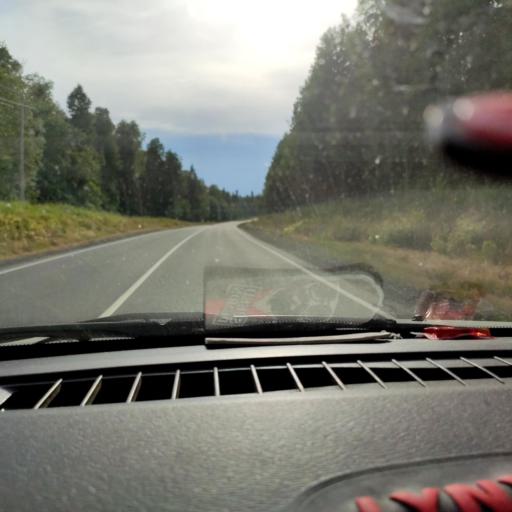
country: RU
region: Perm
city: Perm
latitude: 58.1942
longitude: 56.2475
